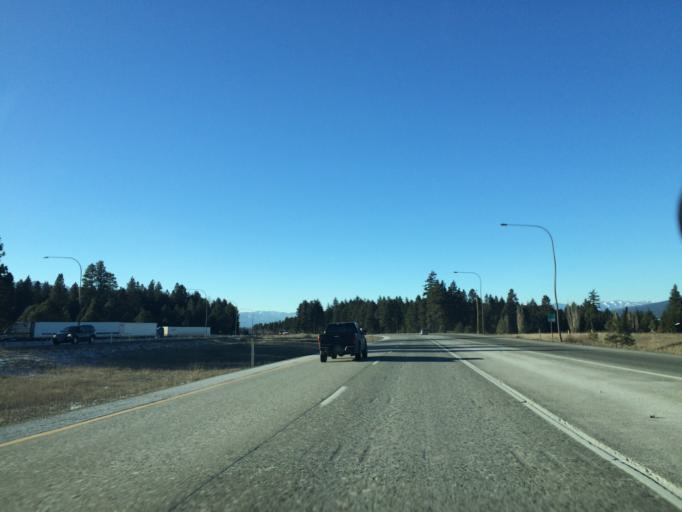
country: US
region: Washington
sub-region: Kittitas County
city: Cle Elum
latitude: 47.1614
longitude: -120.8460
